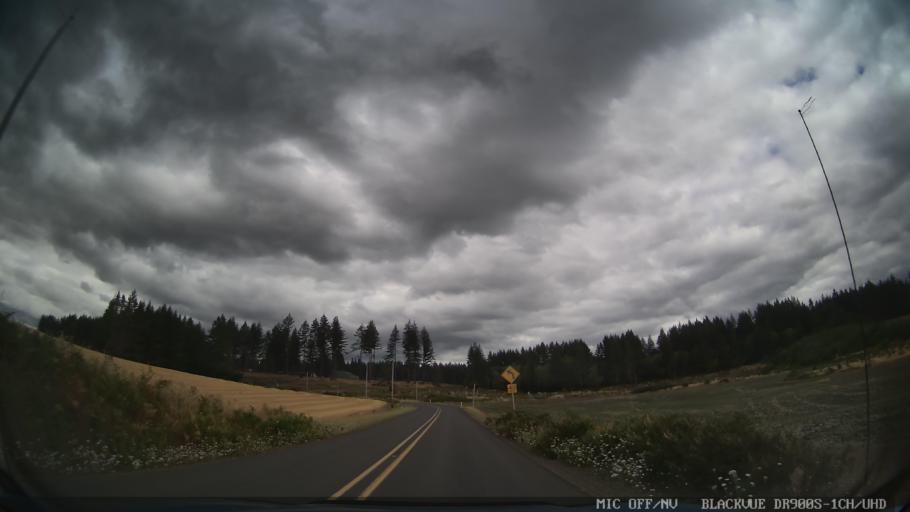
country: US
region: Oregon
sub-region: Linn County
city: Lyons
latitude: 44.8484
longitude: -122.6667
